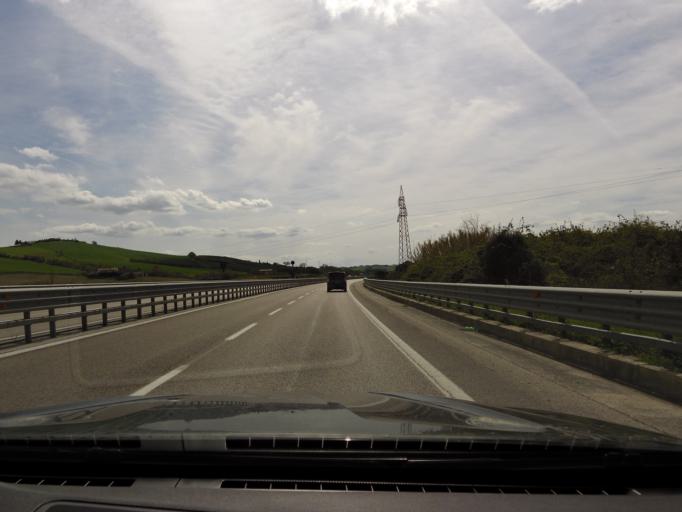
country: IT
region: The Marches
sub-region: Provincia di Ancona
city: Ancona
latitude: 43.5544
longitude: 13.5175
